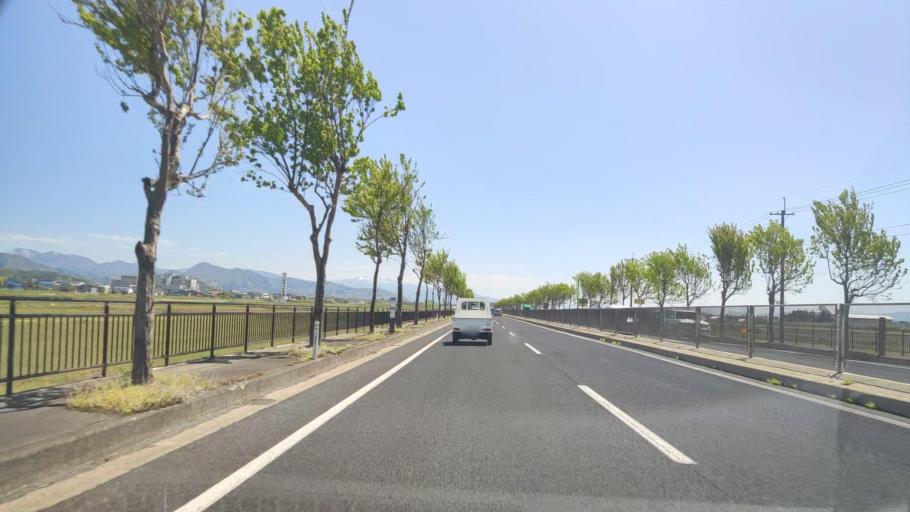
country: JP
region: Yamagata
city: Higashine
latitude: 38.4705
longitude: 140.3828
